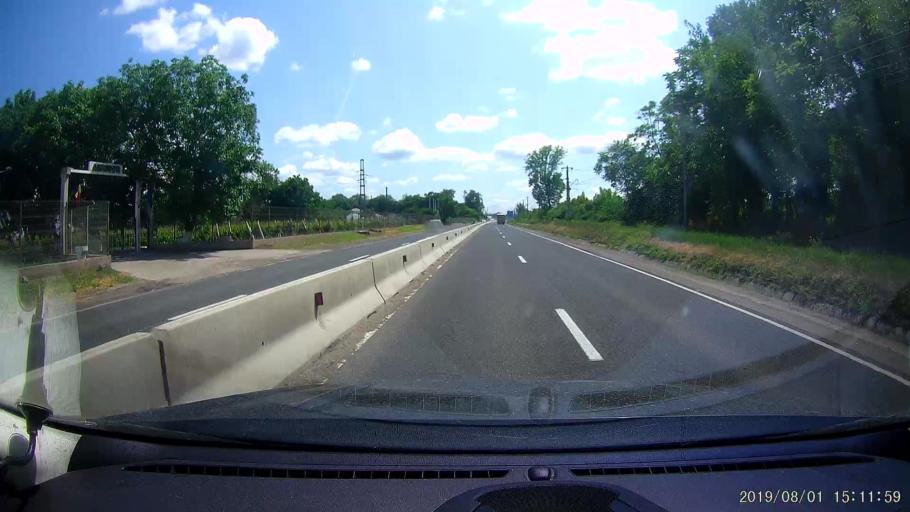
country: RO
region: Braila
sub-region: Comuna Chiscani
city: Lacu Sarat
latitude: 45.2113
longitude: 27.9184
